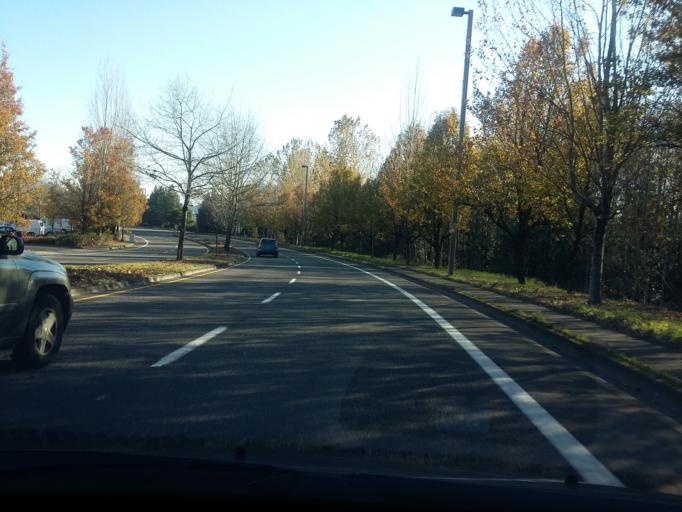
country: US
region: Oregon
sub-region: Multnomah County
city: Fairview
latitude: 45.5599
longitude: -122.5149
